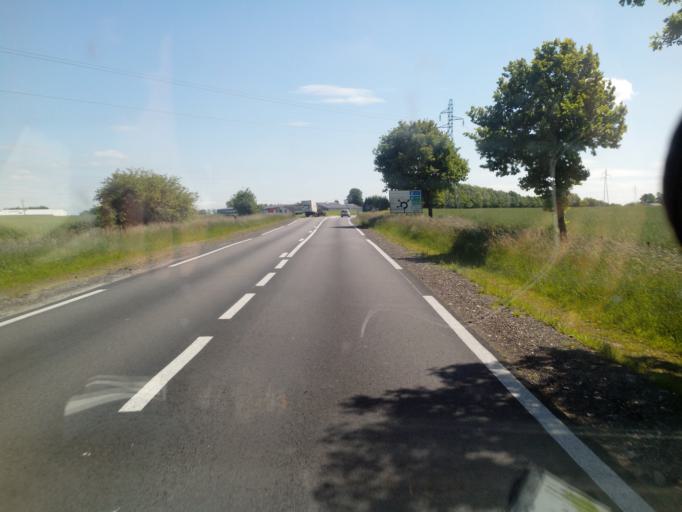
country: FR
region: Haute-Normandie
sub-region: Departement de l'Eure
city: Beuzeville
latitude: 49.3610
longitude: 0.3946
